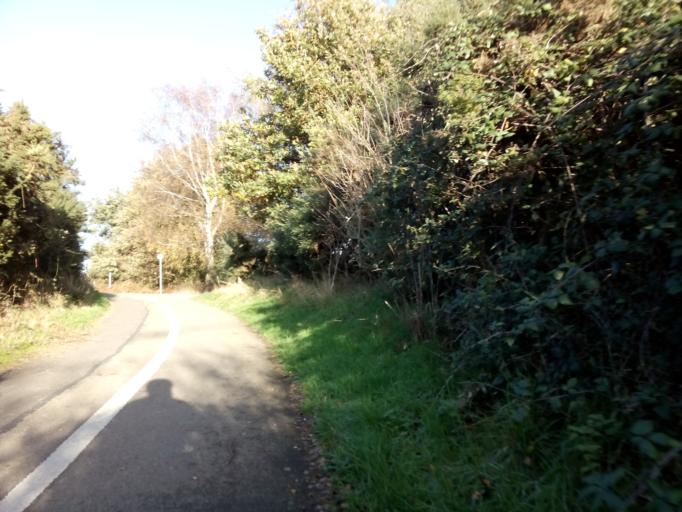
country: GB
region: England
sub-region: Suffolk
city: Kesgrave
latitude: 52.0663
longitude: 1.2748
